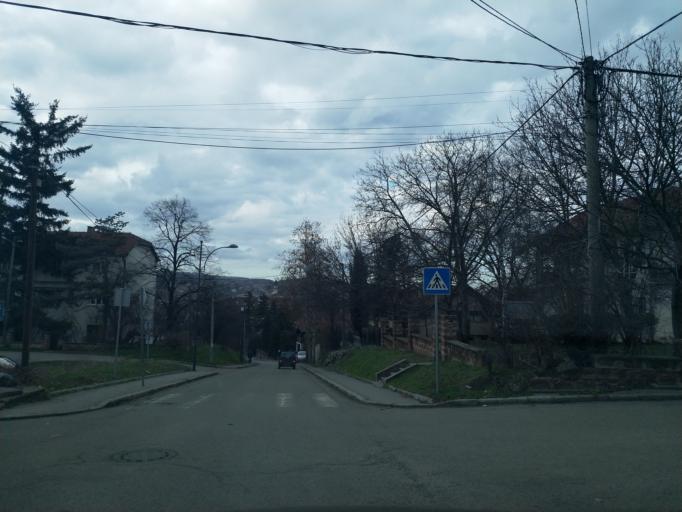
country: RS
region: Central Serbia
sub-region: Belgrade
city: Grocka
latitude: 44.6681
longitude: 20.7200
